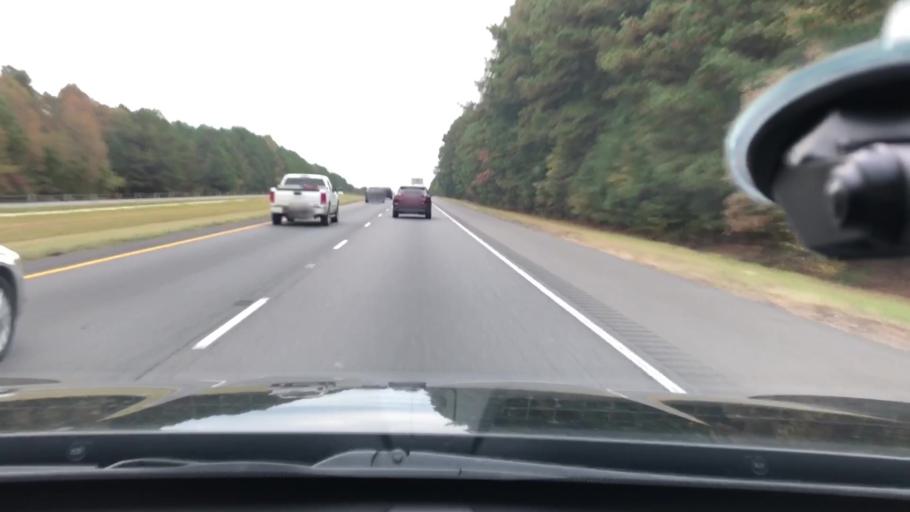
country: US
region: Arkansas
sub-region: Clark County
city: Arkadelphia
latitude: 34.0426
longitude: -93.1391
